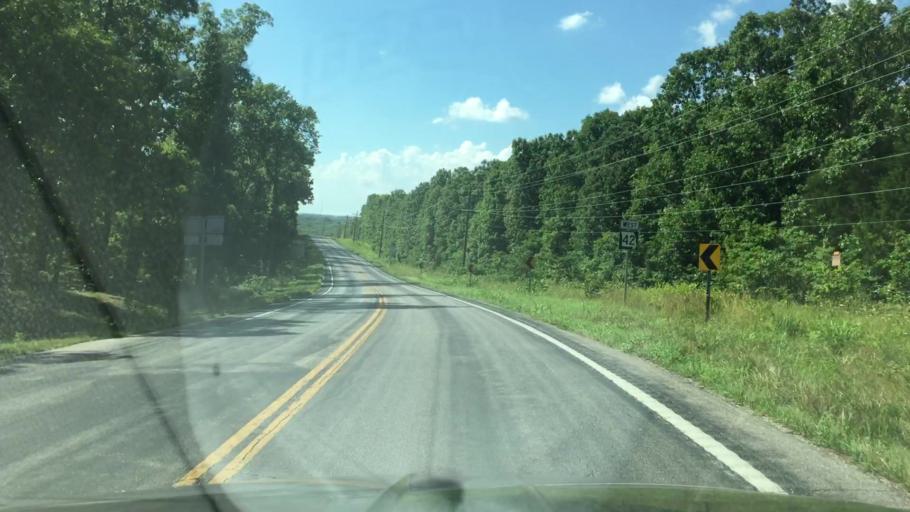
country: US
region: Missouri
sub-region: Camden County
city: Osage Beach
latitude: 38.1307
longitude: -92.5574
